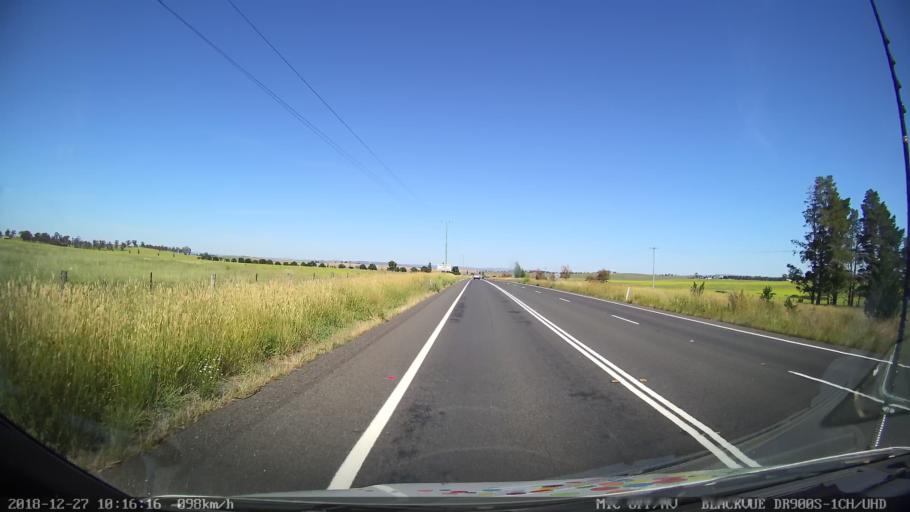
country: AU
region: New South Wales
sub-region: Bathurst Regional
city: Kelso
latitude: -33.4260
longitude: 149.6987
